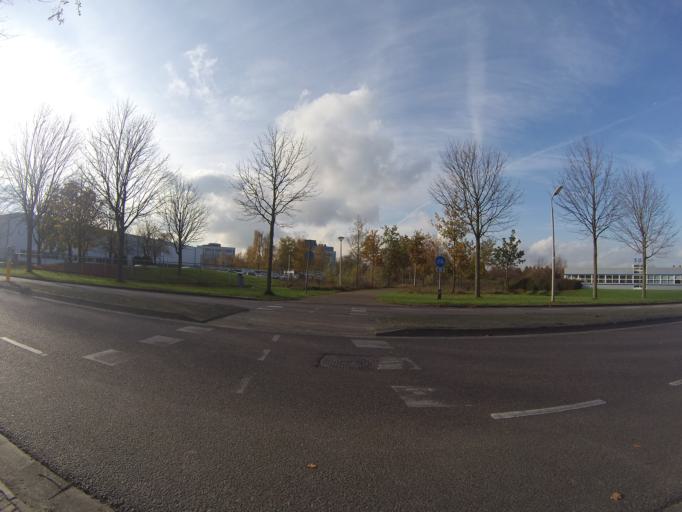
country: NL
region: Utrecht
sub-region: Gemeente Amersfoort
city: Randenbroek
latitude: 52.1778
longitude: 5.4138
